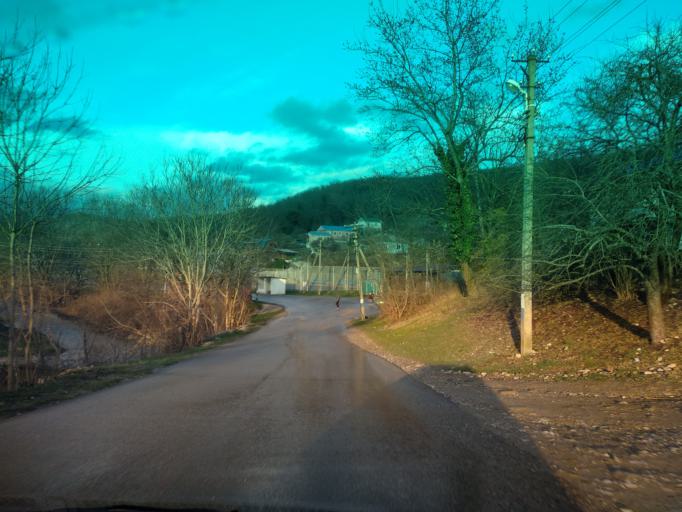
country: RU
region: Krasnodarskiy
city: Novomikhaylovskiy
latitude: 44.2707
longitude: 38.8313
